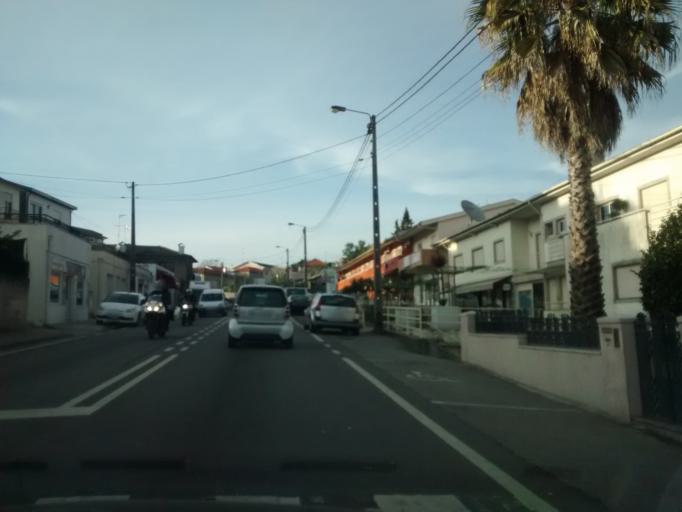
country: PT
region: Braga
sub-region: Guimaraes
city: Guimaraes
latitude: 41.4584
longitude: -8.3118
